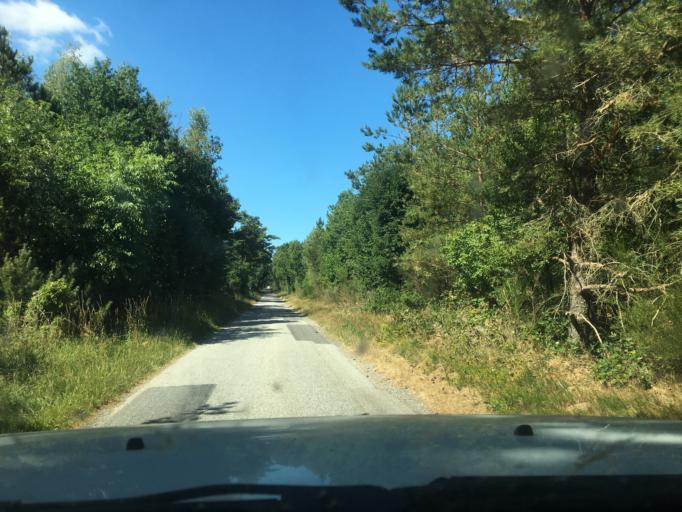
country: DK
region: Central Jutland
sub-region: Syddjurs Kommune
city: Ryomgard
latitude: 56.4856
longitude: 10.5940
